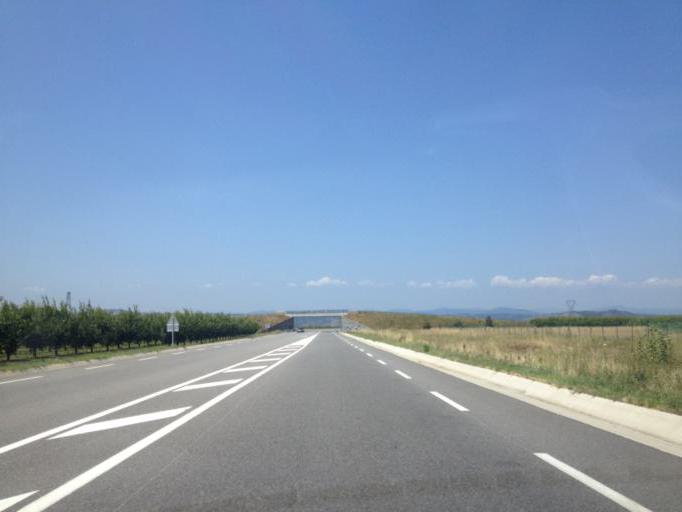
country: FR
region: Rhone-Alpes
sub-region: Departement de la Drome
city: Chanos-Curson
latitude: 45.0542
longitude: 4.9153
